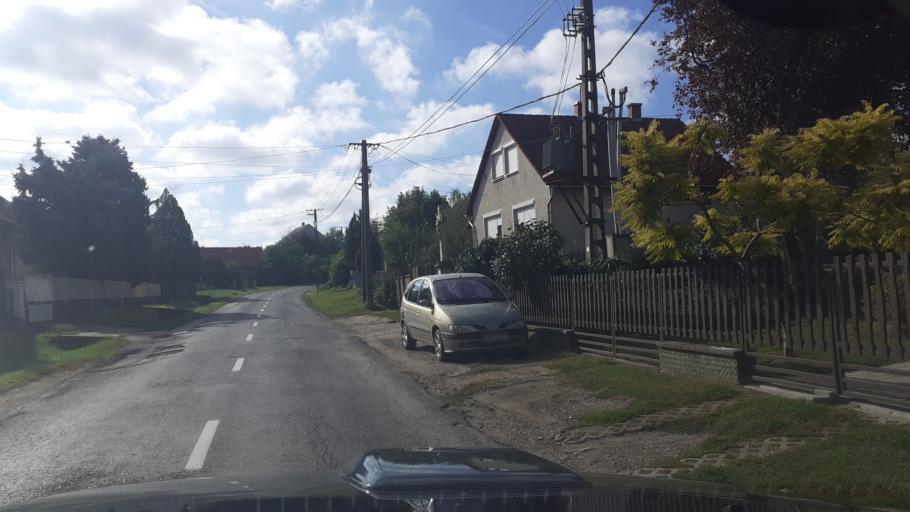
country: HU
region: Fejer
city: Baracs
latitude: 46.8979
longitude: 18.8978
